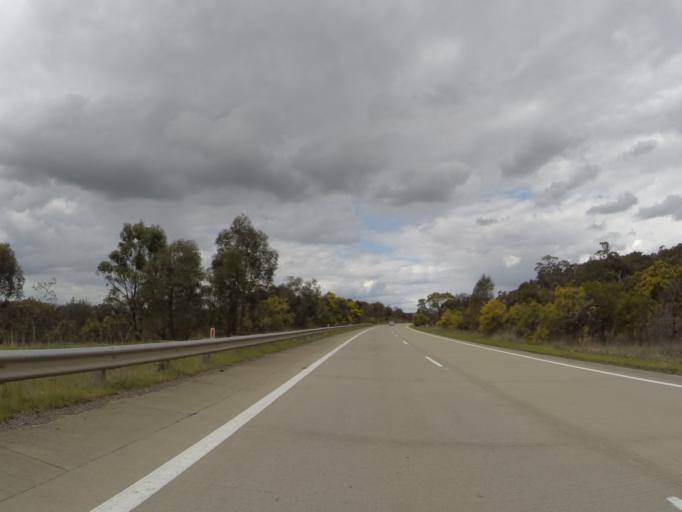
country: AU
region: New South Wales
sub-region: Goulburn Mulwaree
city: Goulburn
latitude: -34.8032
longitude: 149.4956
